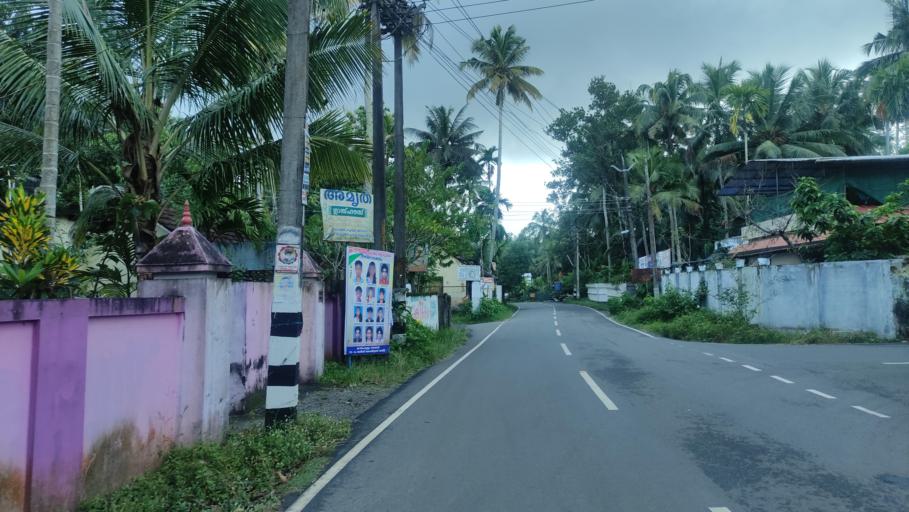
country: IN
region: Kerala
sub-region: Alappuzha
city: Kayankulam
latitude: 9.1944
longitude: 76.5025
